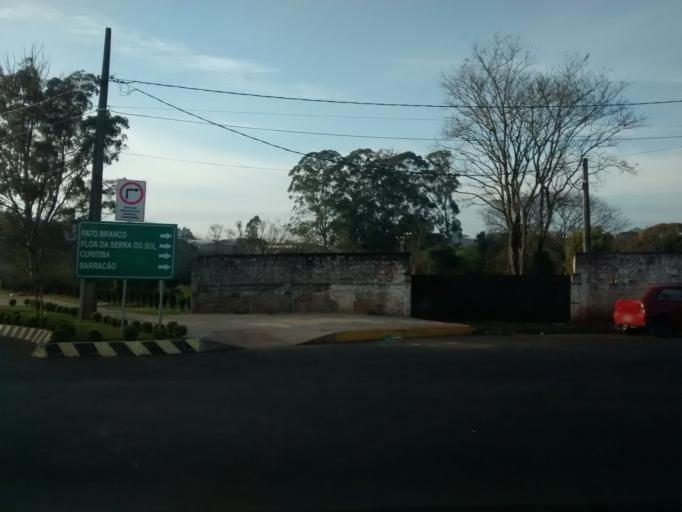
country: BR
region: Parana
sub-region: Francisco Beltrao
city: Francisco Beltrao
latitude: -26.1506
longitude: -53.0214
